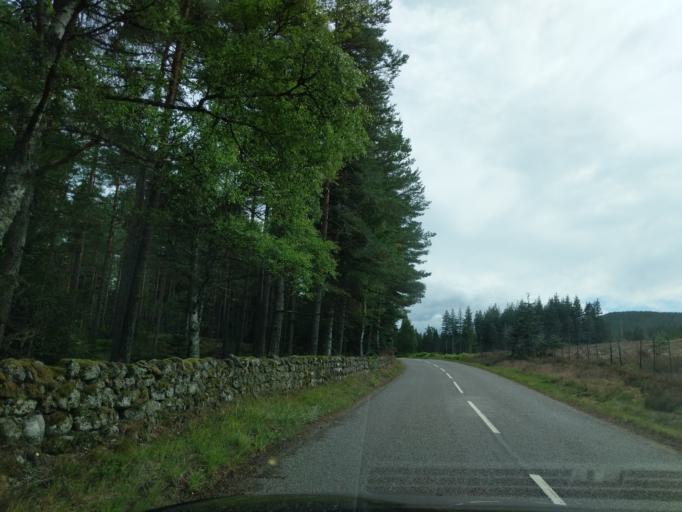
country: GB
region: Scotland
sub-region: Aberdeenshire
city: Aboyne
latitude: 57.0645
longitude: -2.8124
